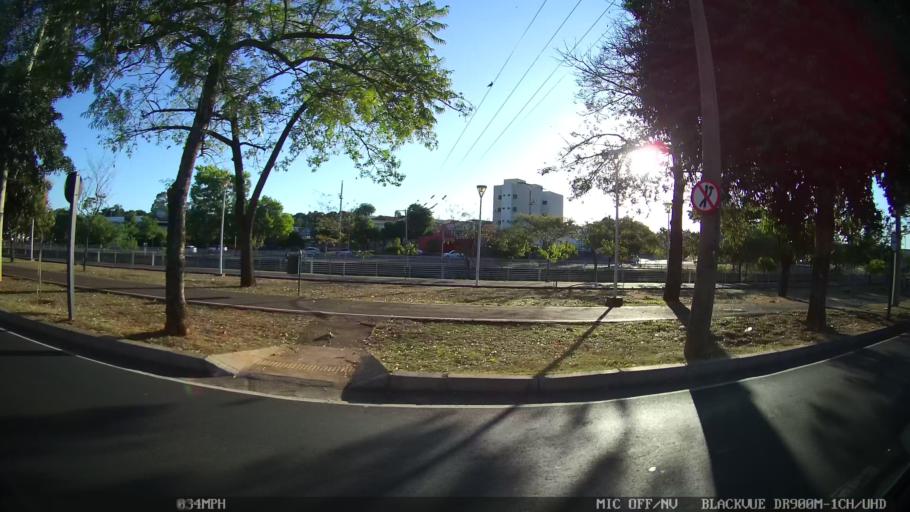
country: BR
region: Sao Paulo
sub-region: Sao Jose Do Rio Preto
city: Sao Jose do Rio Preto
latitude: -20.7871
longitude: -49.3763
